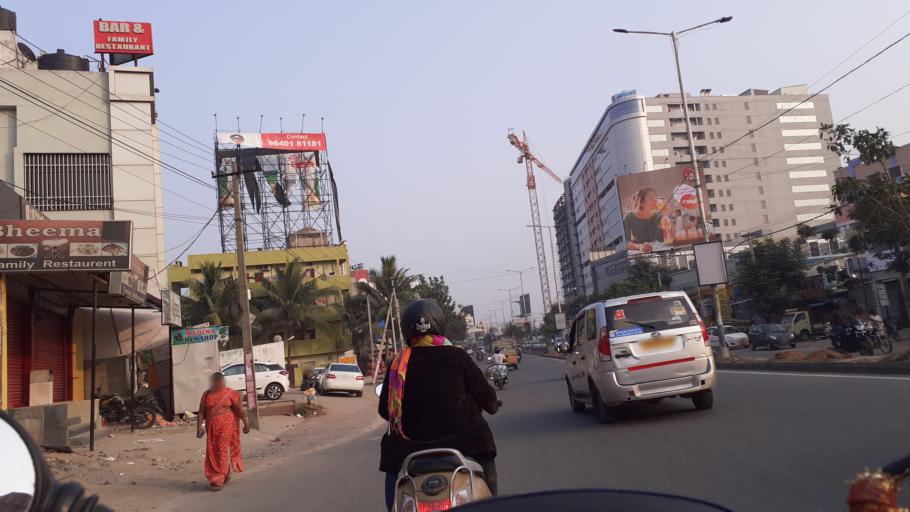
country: IN
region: Telangana
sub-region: Medak
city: Serilingampalle
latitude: 17.4870
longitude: 78.3572
